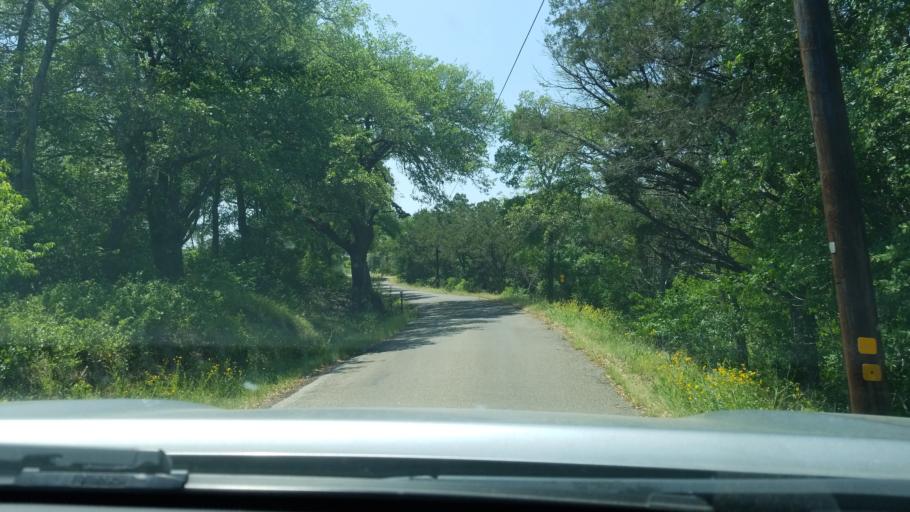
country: US
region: Texas
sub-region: Blanco County
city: Blanco
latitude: 30.0013
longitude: -98.4071
